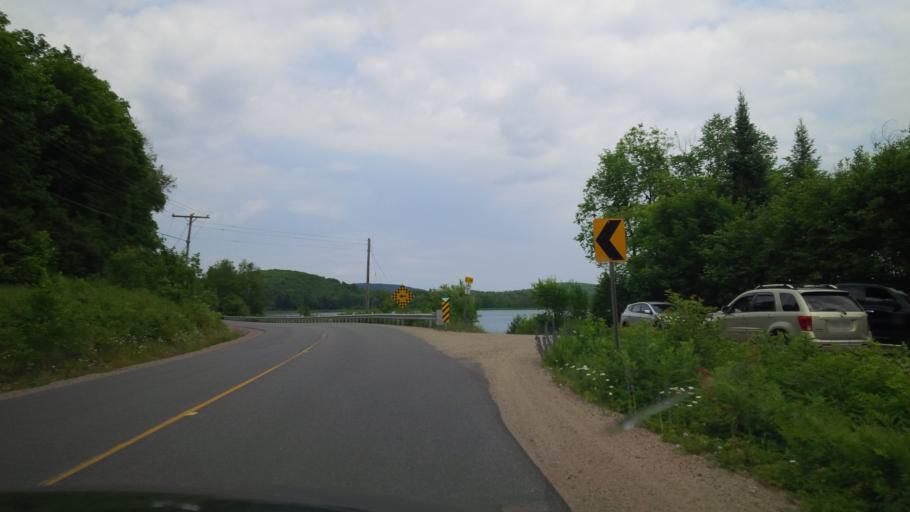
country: CA
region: Ontario
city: Huntsville
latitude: 45.5790
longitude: -79.2162
